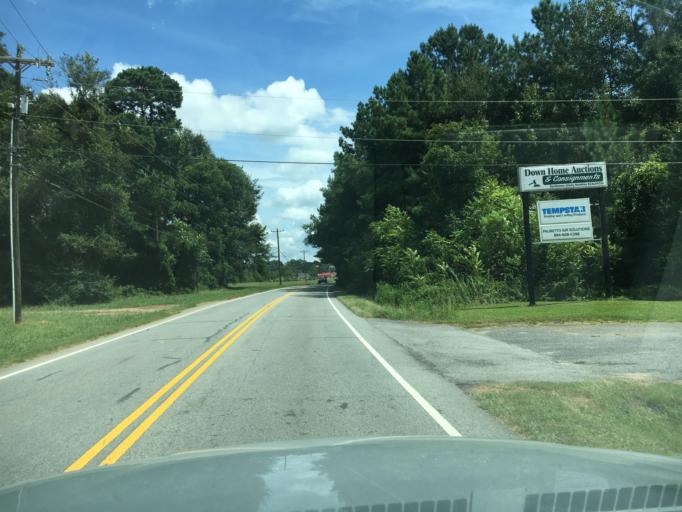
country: US
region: South Carolina
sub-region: Anderson County
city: Williamston
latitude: 34.6172
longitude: -82.5084
